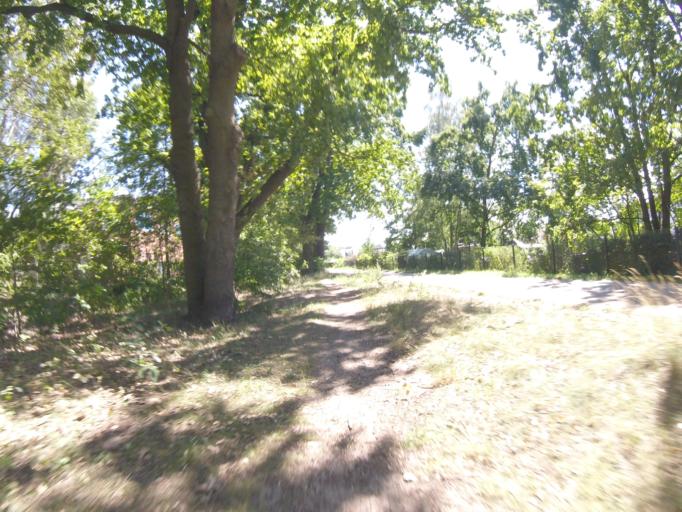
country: DE
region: Brandenburg
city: Konigs Wusterhausen
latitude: 52.2851
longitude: 13.6100
